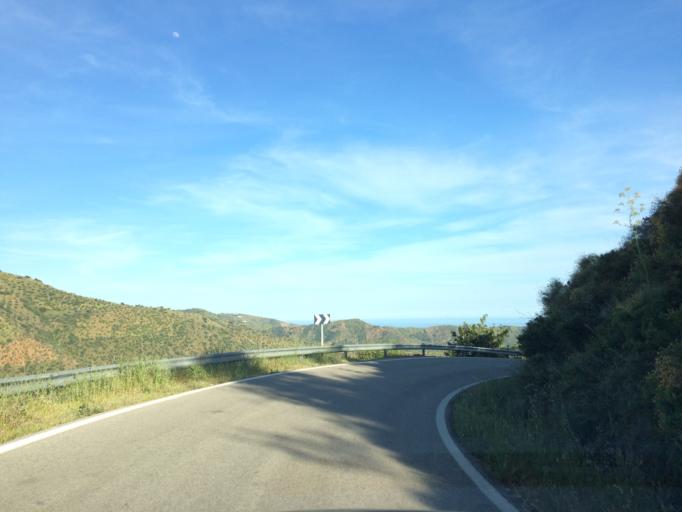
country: ES
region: Andalusia
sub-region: Provincia de Malaga
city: Totalan
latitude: 36.7793
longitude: -4.3173
